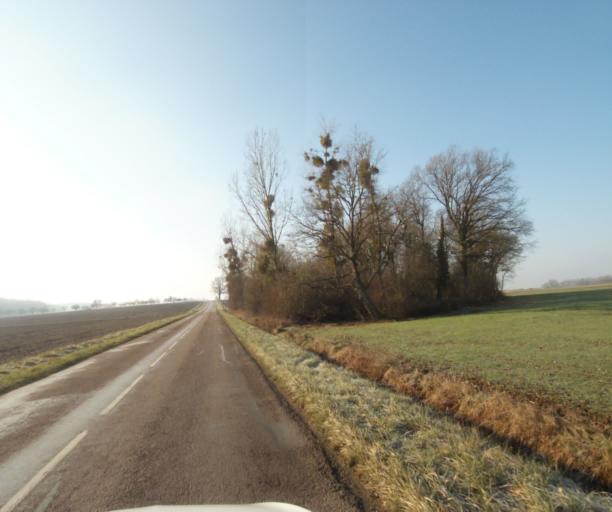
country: FR
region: Champagne-Ardenne
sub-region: Departement de la Haute-Marne
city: Montier-en-Der
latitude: 48.4449
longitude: 4.7602
